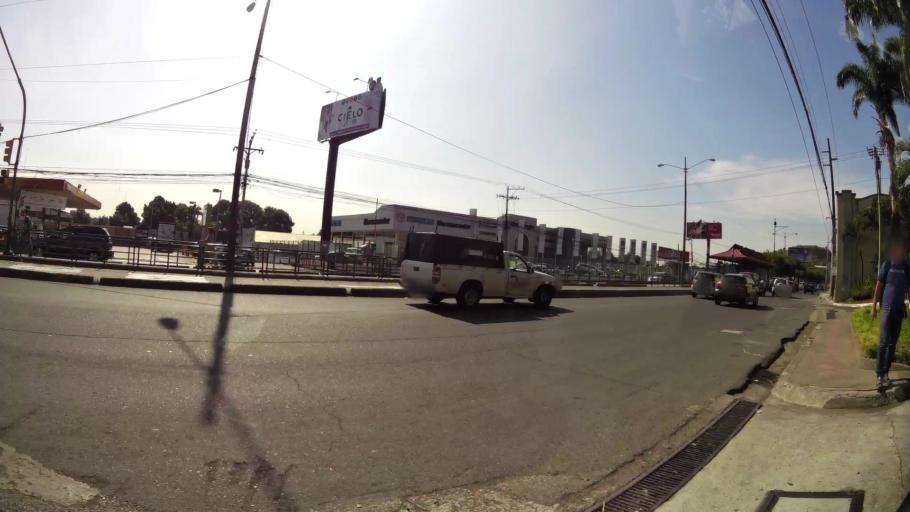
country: EC
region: Guayas
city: Guayaquil
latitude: -2.1758
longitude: -79.9128
